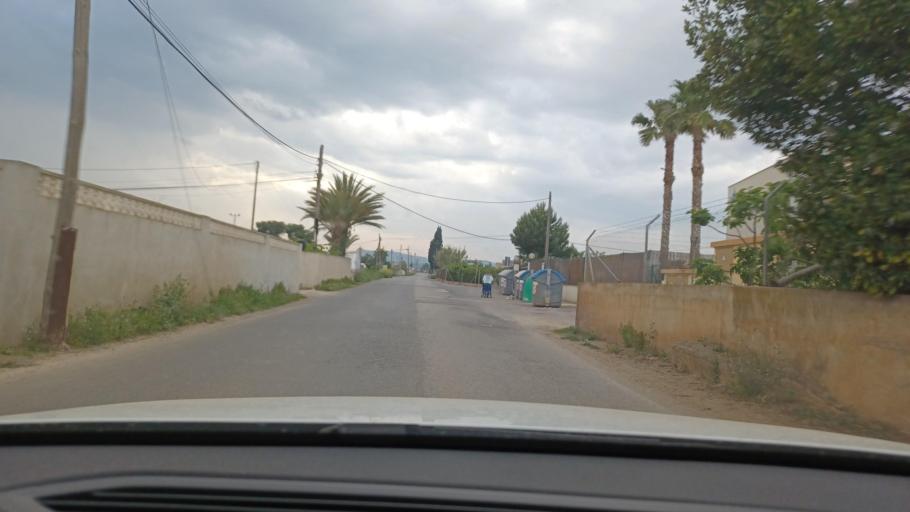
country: ES
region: Valencia
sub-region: Provincia de Castello
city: Benicarlo
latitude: 40.4036
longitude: 0.4080
